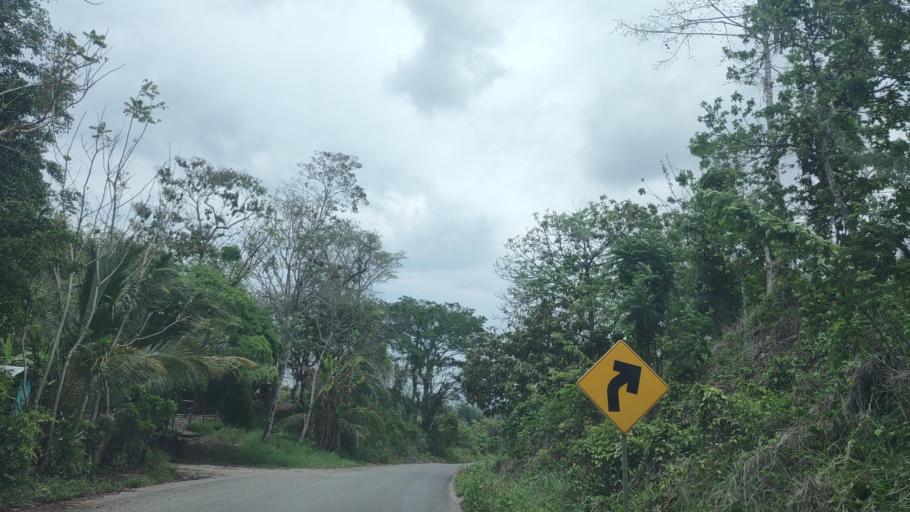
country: MX
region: Tabasco
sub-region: Huimanguillo
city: Francisco Rueda
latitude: 17.5237
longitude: -94.1350
